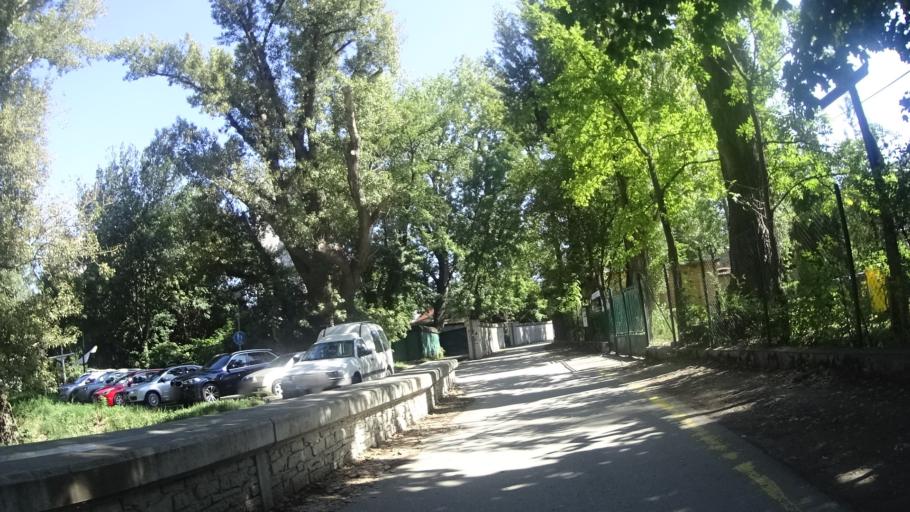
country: SK
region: Bratislavsky
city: Bratislava
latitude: 48.1454
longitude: 17.0698
